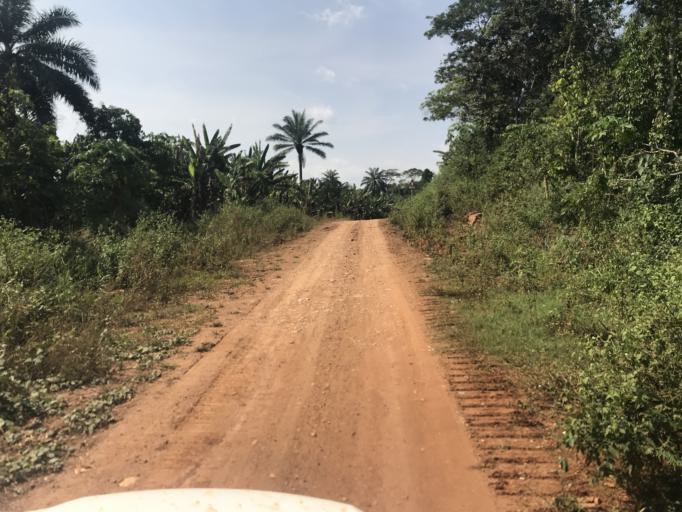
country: NG
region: Osun
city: Ilesa
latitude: 7.6315
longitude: 4.6794
